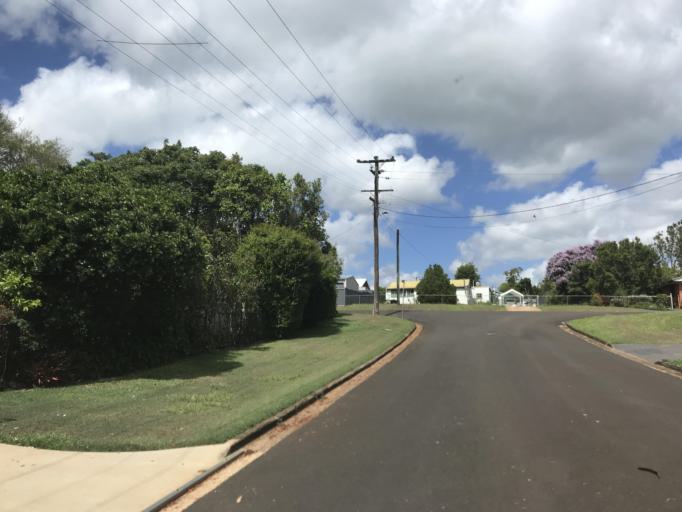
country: AU
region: Queensland
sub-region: Tablelands
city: Tolga
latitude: -17.2241
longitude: 145.4756
